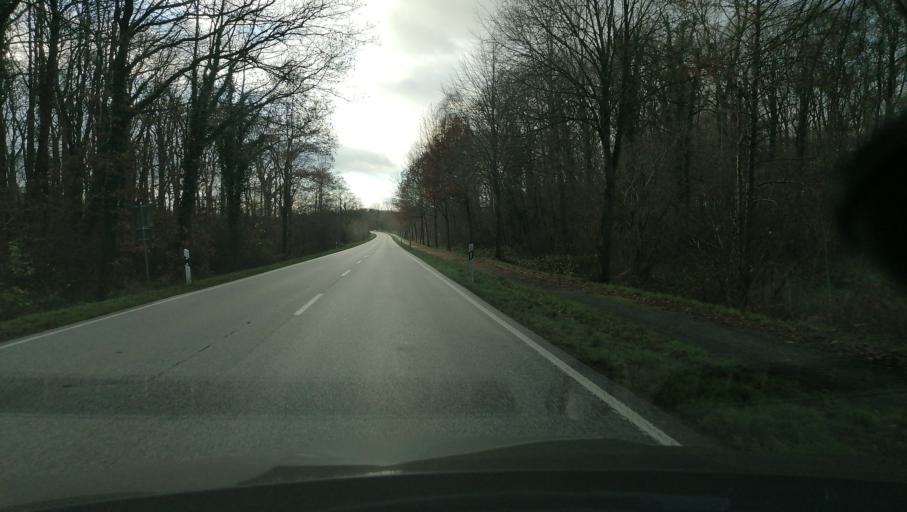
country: DE
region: Schleswig-Holstein
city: Tensbuttel-Rost
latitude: 54.1119
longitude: 9.2139
